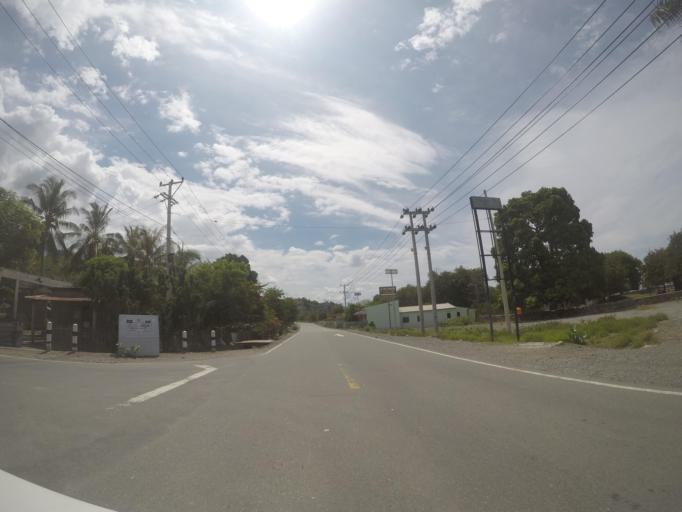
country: TL
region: Liquica
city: Liquica
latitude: -8.5702
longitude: 125.3815
